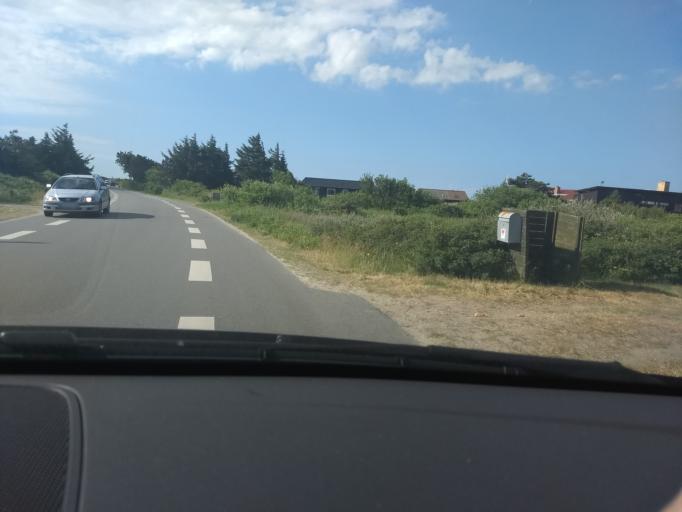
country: DE
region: Schleswig-Holstein
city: List
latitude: 55.1436
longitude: 8.4942
